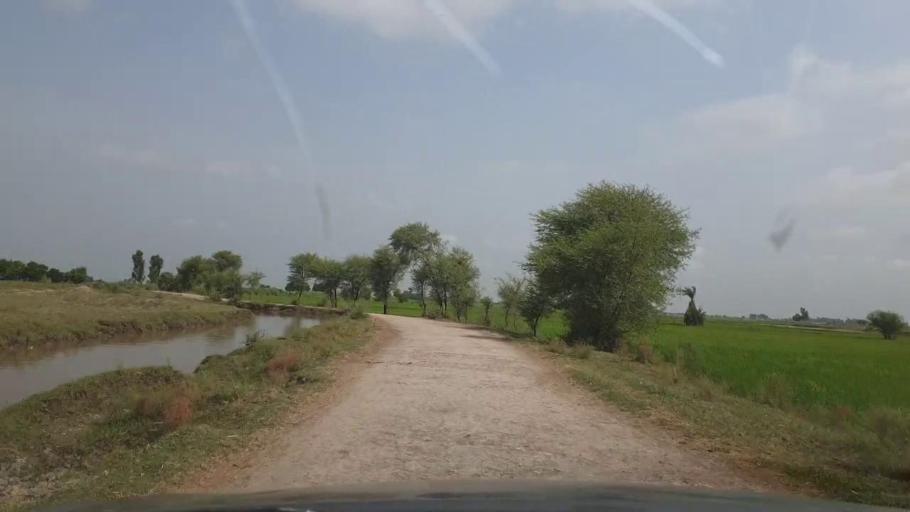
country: PK
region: Sindh
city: Ratodero
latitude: 27.8452
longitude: 68.3080
